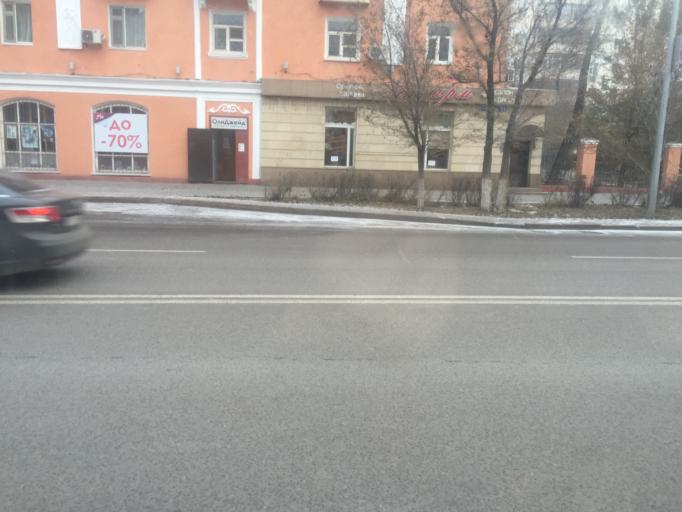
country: KZ
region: Astana Qalasy
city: Astana
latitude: 51.1910
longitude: 71.4087
